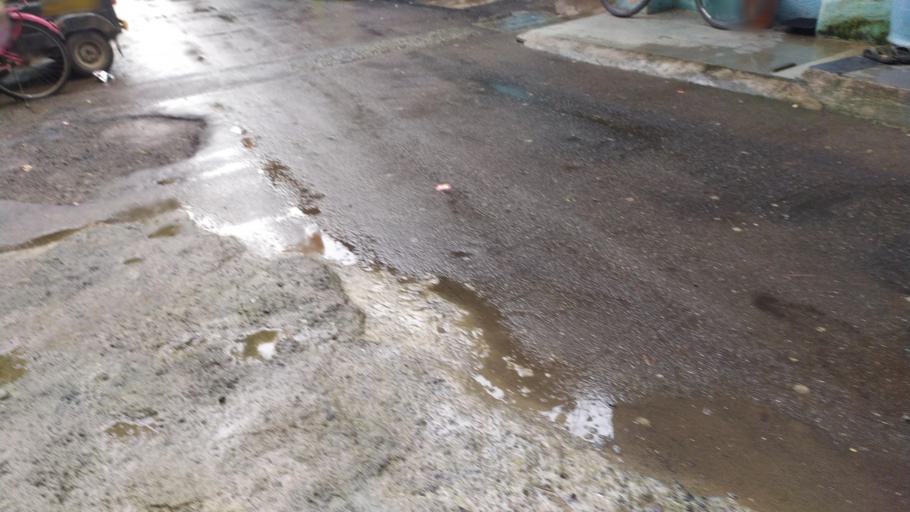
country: IN
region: Maharashtra
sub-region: Mumbai Suburban
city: Borivli
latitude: 19.2399
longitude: 72.8564
